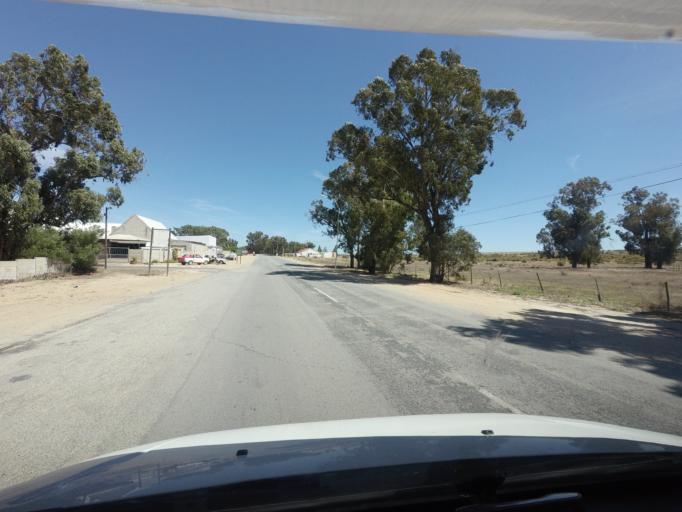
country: ZA
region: Western Cape
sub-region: West Coast District Municipality
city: Vredenburg
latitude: -32.7901
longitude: 18.2056
